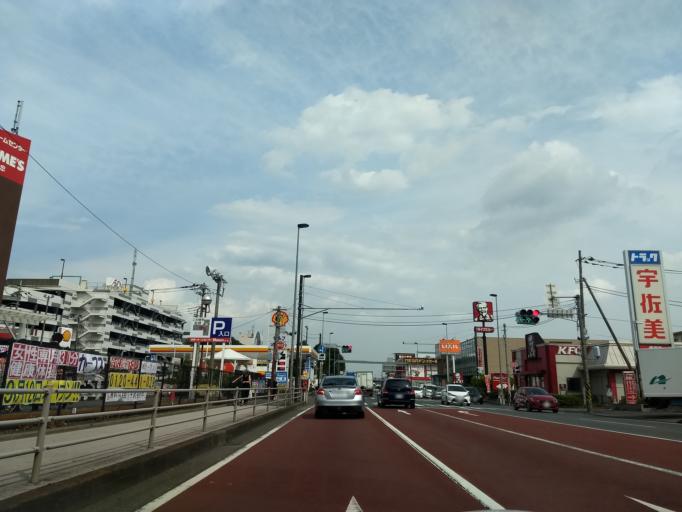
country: JP
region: Tokyo
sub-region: Machida-shi
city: Machida
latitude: 35.5542
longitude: 139.4141
